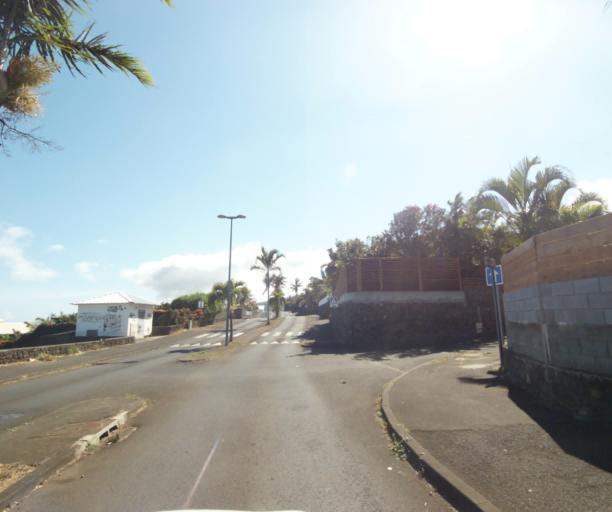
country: RE
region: Reunion
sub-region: Reunion
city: Saint-Paul
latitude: -20.9909
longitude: 55.3278
